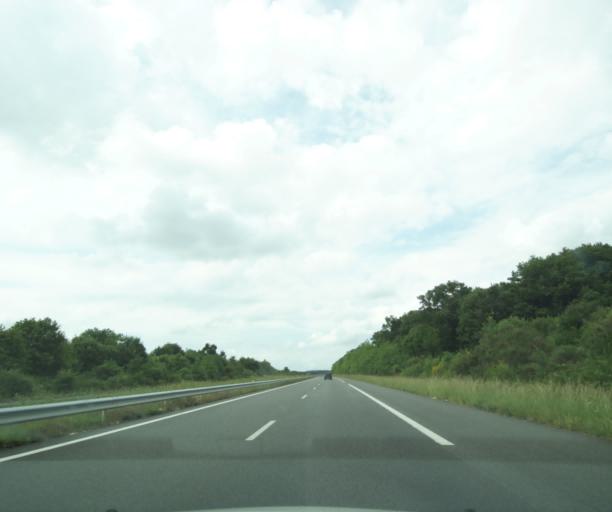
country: FR
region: Centre
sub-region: Departement du Cher
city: Orval
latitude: 46.7974
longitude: 2.4137
